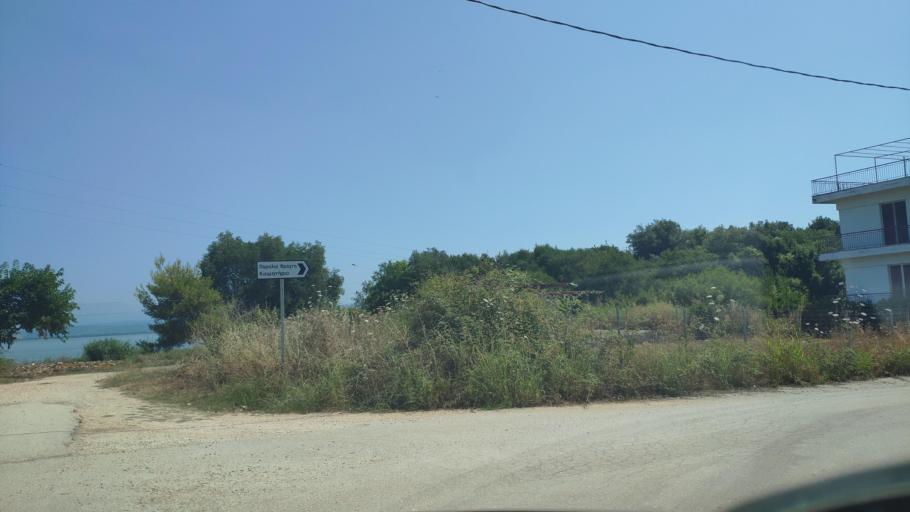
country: GR
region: Epirus
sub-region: Nomos Artas
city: Aneza
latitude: 39.0132
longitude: 20.9215
